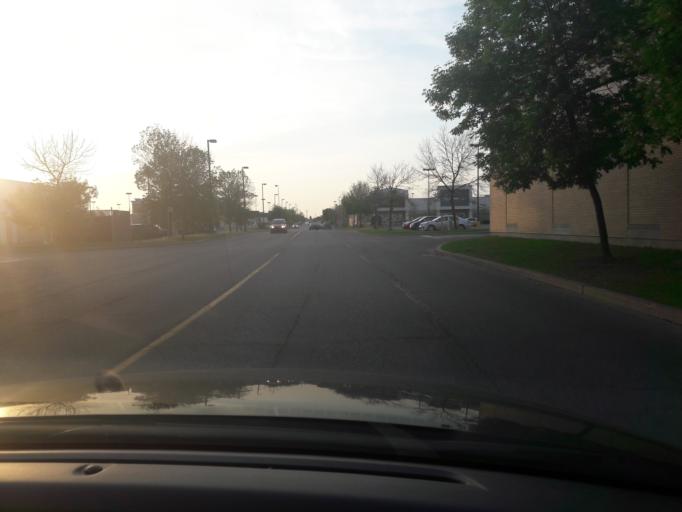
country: CA
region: Quebec
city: Dollard-Des Ormeaux
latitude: 45.5255
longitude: -73.7810
